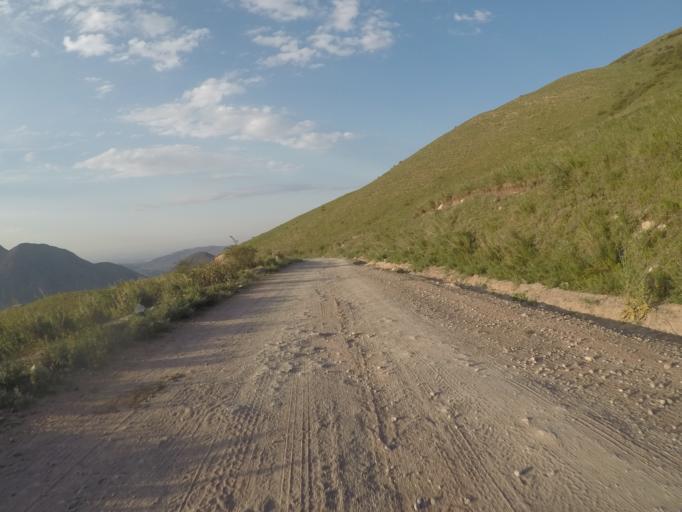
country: KG
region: Chuy
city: Bishkek
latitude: 42.6539
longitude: 74.6626
